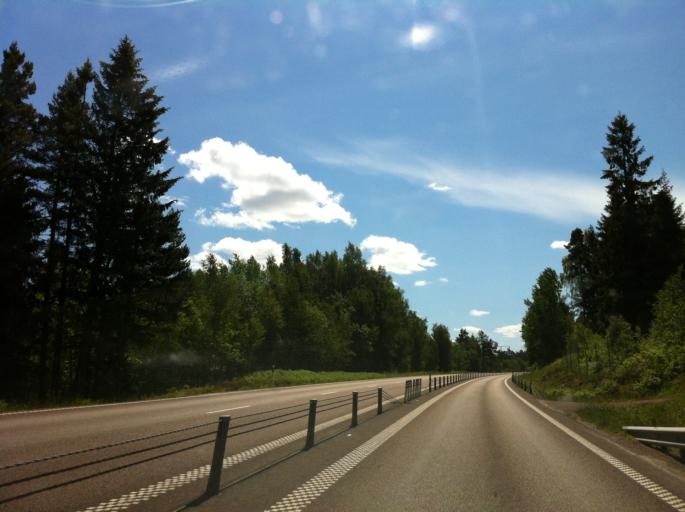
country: SE
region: Vaestra Goetaland
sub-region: Melleruds Kommun
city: Mellerud
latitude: 58.8126
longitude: 12.5238
